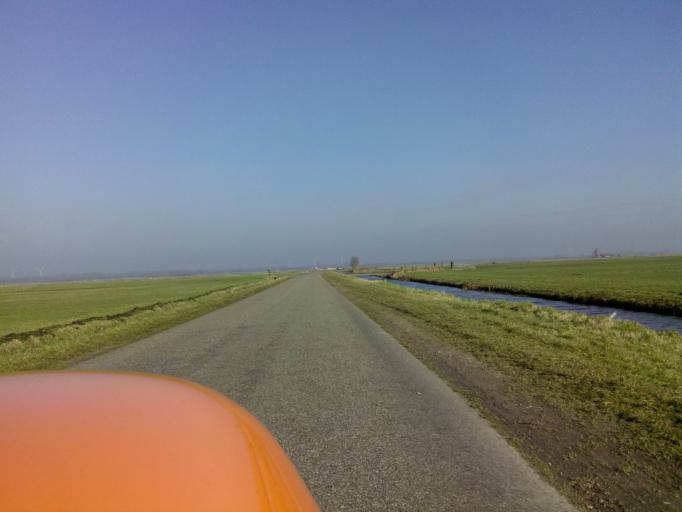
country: NL
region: Utrecht
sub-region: Gemeente Bunschoten
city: Bunschoten
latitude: 52.2305
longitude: 5.4258
